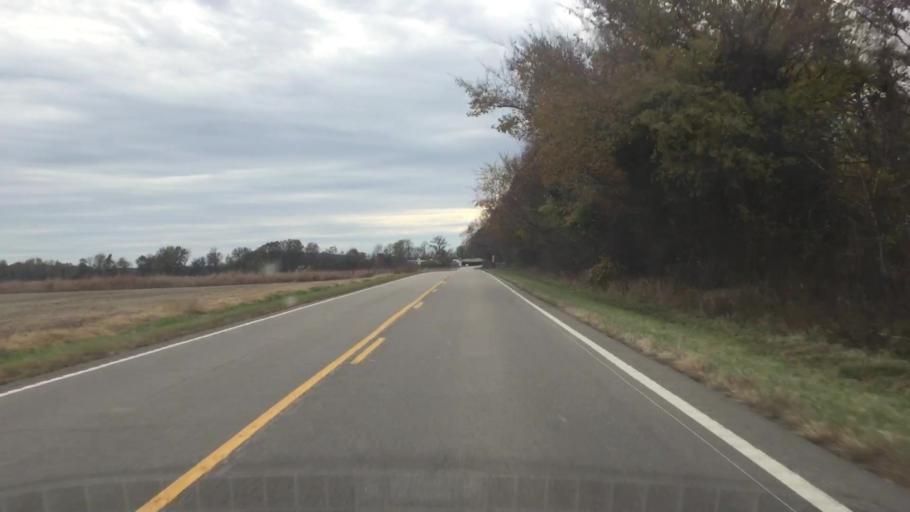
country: US
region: Missouri
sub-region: Callaway County
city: Holts Summit
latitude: 38.6145
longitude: -91.9719
